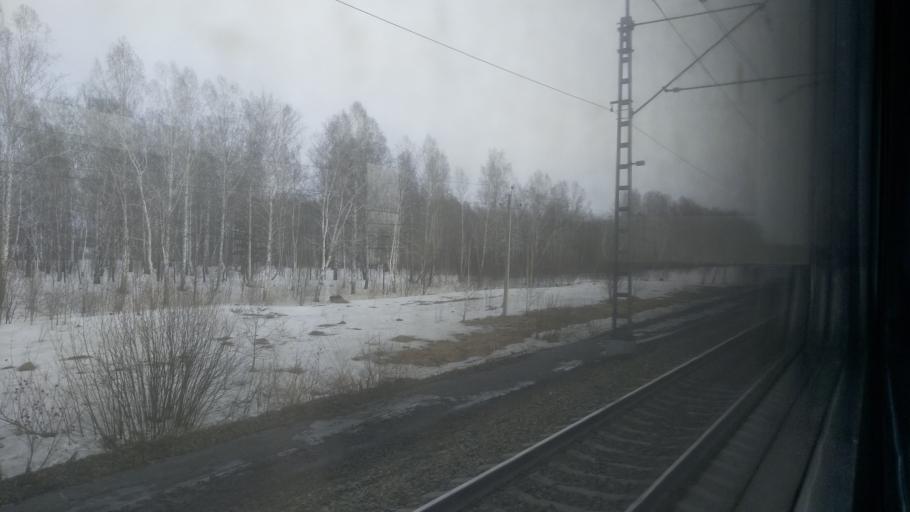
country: RU
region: Novosibirsk
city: Stantsionno-Oyashinskiy
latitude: 55.5056
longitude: 83.9224
